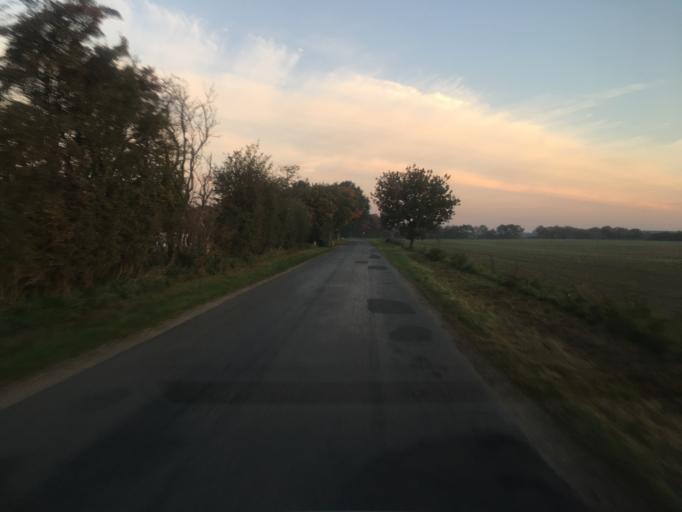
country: DE
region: Schleswig-Holstein
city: Bramstedtlund
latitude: 54.9803
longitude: 9.0667
